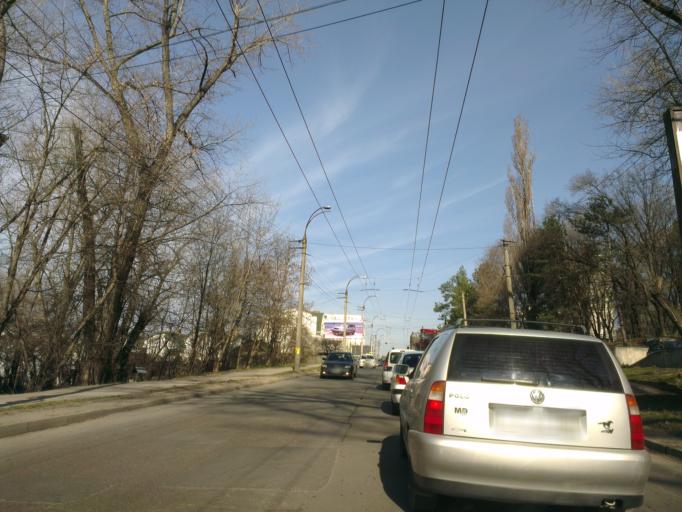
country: MD
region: Chisinau
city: Chisinau
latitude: 47.0373
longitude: 28.8602
